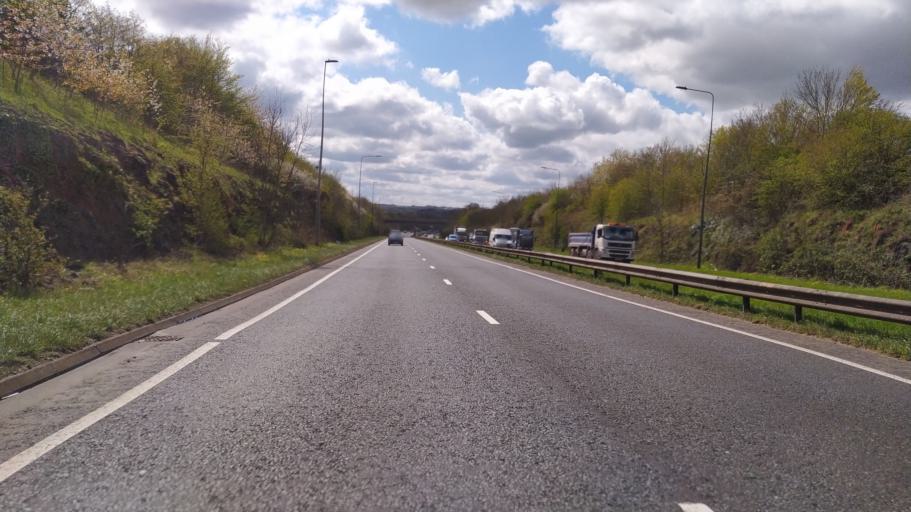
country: GB
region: England
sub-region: South Gloucestershire
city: Kingswood
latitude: 51.4364
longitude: -2.5106
